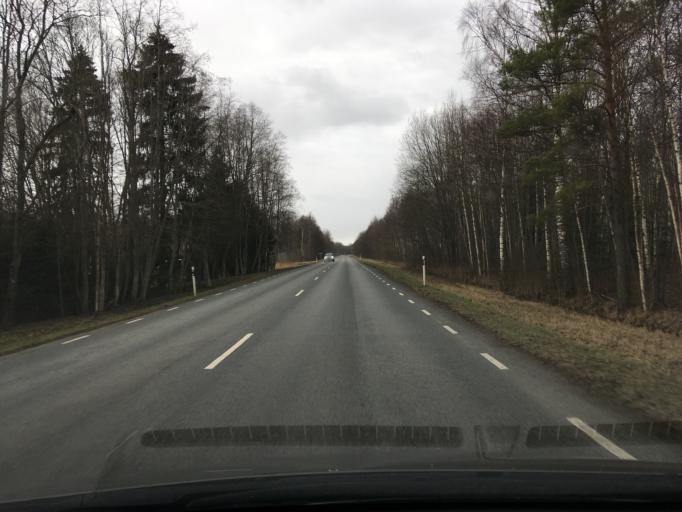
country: EE
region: Laeaene
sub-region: Lihula vald
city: Lihula
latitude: 58.6431
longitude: 23.8520
